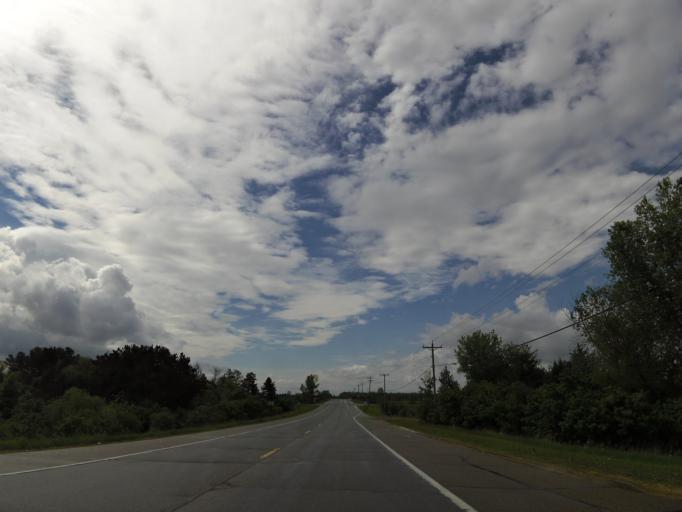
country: US
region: Minnesota
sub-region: Washington County
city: Lakeland
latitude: 44.9586
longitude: -92.7968
